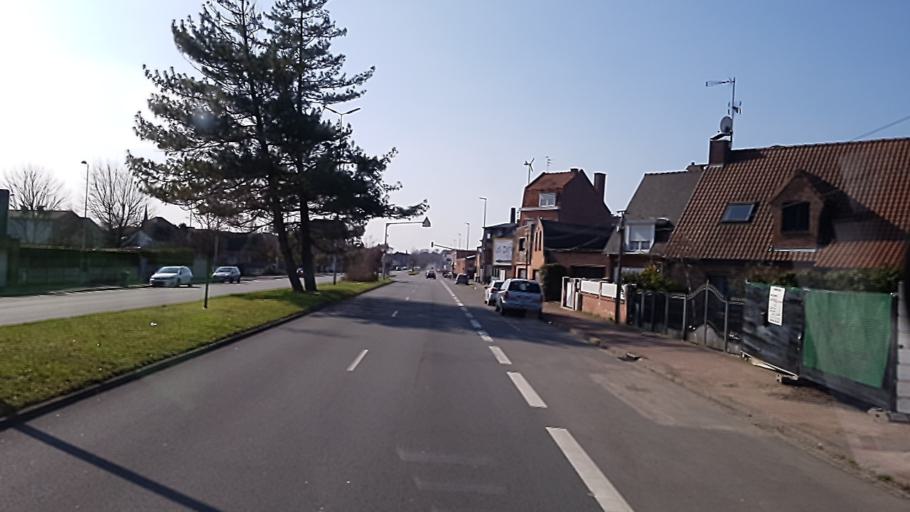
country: FR
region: Nord-Pas-de-Calais
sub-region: Departement du Nord
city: Tourcoing
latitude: 50.7299
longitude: 3.1837
